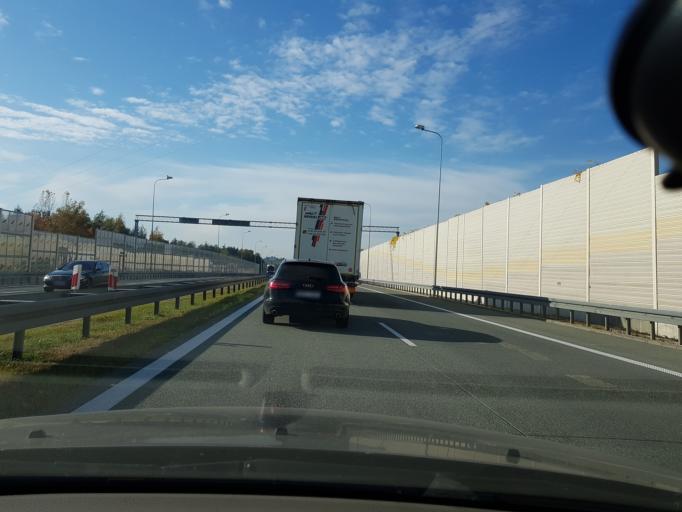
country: PL
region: Lodz Voivodeship
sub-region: Powiat skierniewicki
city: Kowiesy
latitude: 51.8912
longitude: 20.4217
